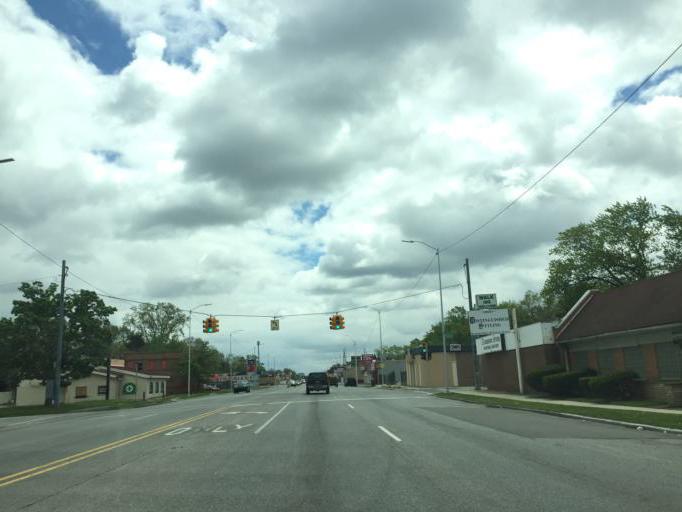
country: US
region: Michigan
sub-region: Wayne County
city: Redford
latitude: 42.4113
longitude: -83.2448
